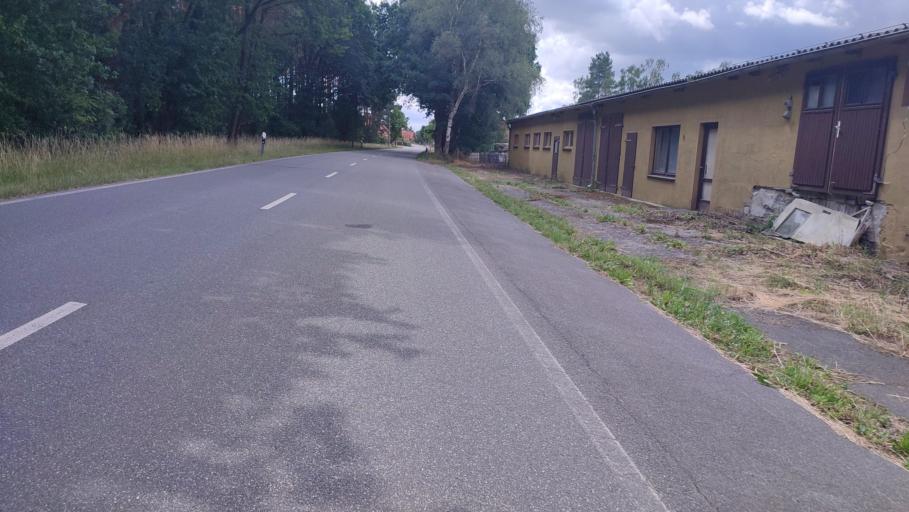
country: DE
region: Lower Saxony
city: Hitzacker
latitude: 53.1882
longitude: 11.1054
